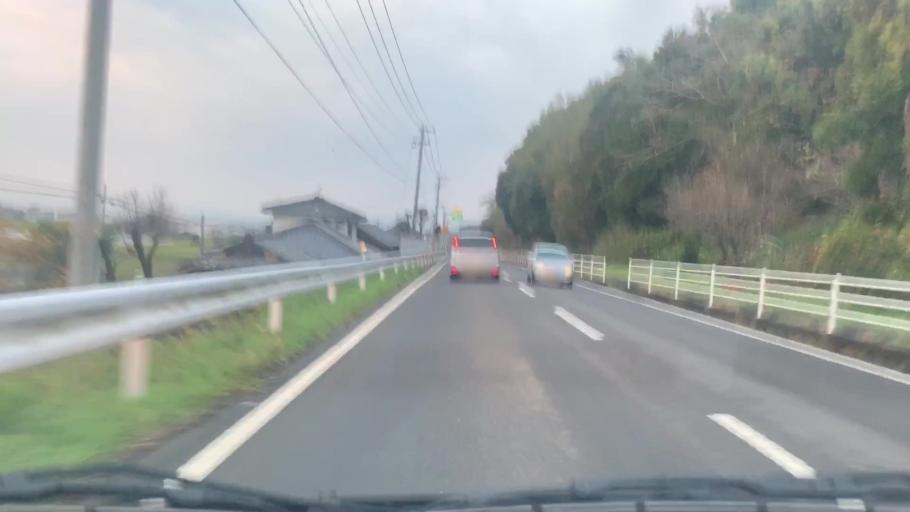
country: JP
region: Saga Prefecture
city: Ureshinomachi-shimojuku
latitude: 33.0497
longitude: 129.9254
